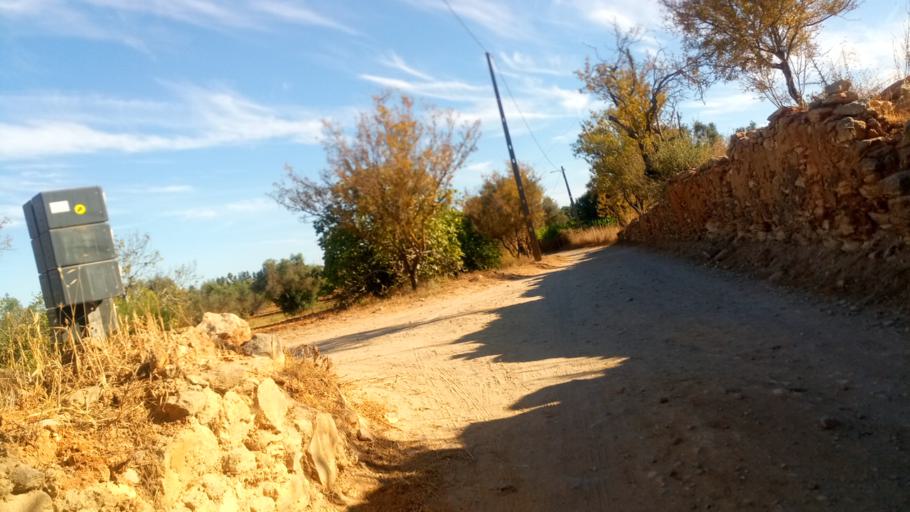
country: PT
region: Faro
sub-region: Tavira
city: Tavira
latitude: 37.1423
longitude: -7.5943
